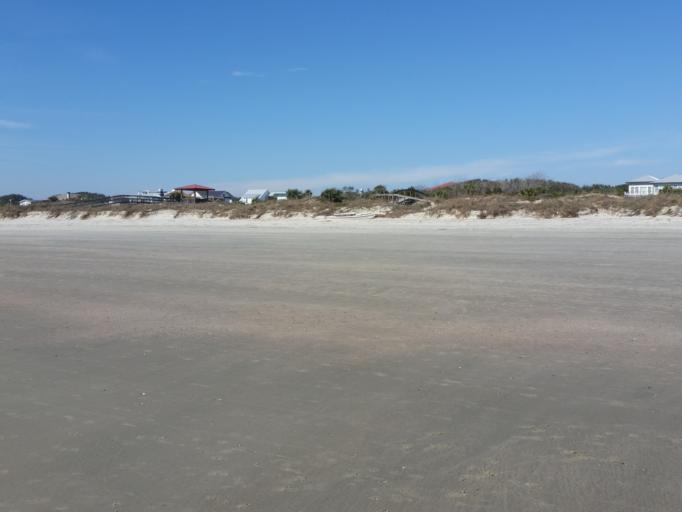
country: US
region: South Carolina
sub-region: Charleston County
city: Isle of Palms
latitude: 32.7891
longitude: -79.7762
